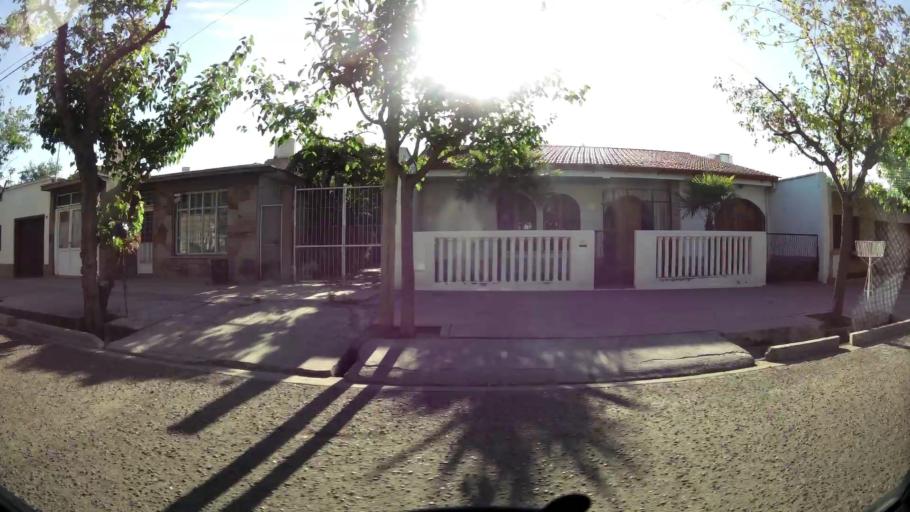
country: AR
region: Mendoza
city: Mendoza
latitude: -32.9018
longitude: -68.8210
